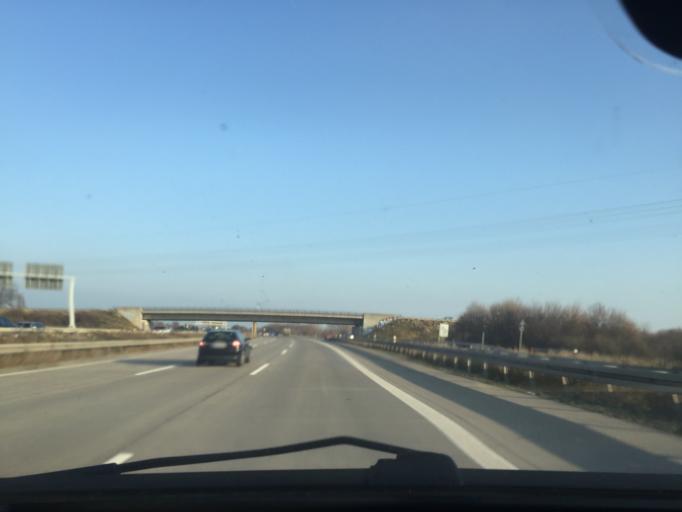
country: DE
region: Saxony-Anhalt
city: Barleben
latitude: 52.1874
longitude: 11.6223
